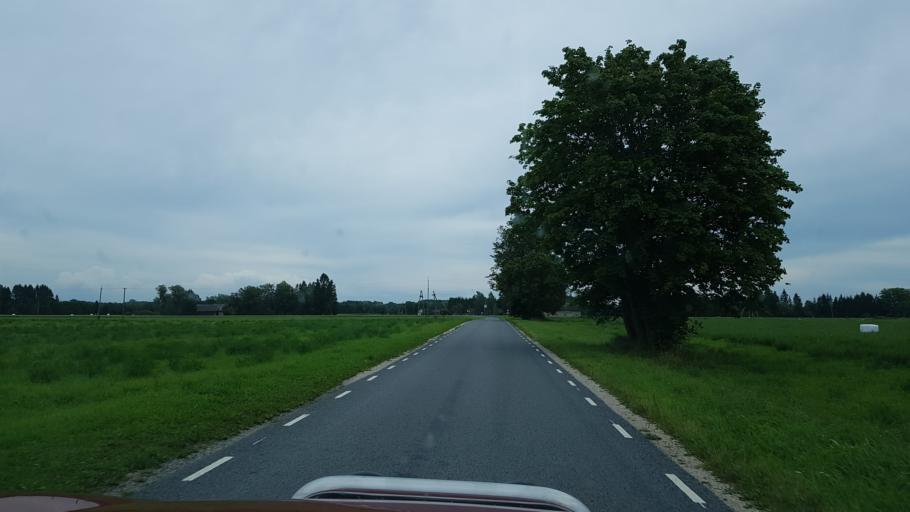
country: EE
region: Harju
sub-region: Nissi vald
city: Turba
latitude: 58.8771
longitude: 24.0811
